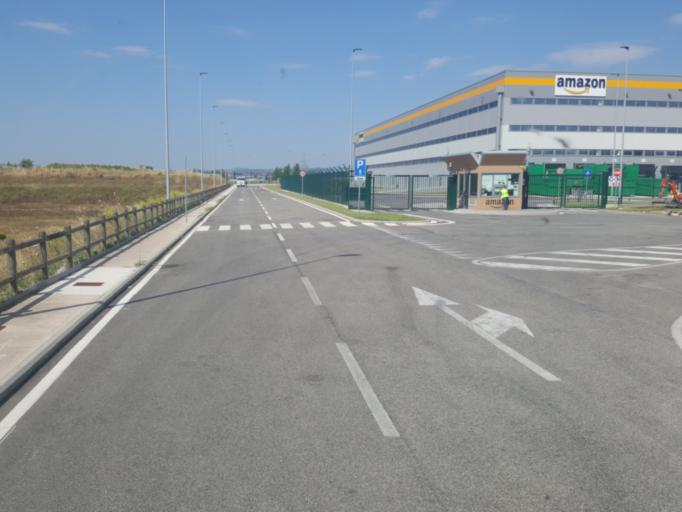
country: IT
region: Latium
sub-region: Citta metropolitana di Roma Capitale
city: Fiano Romano
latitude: 42.1676
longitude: 12.6470
